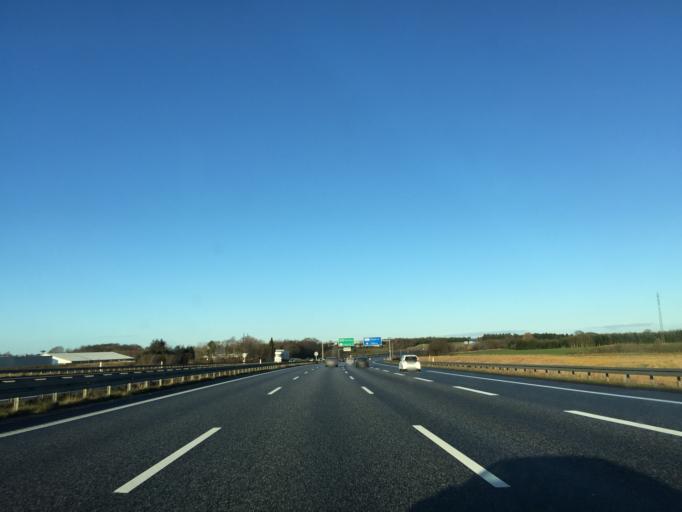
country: DK
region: South Denmark
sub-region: Vejle Kommune
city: Vejle
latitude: 55.6671
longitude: 9.5539
